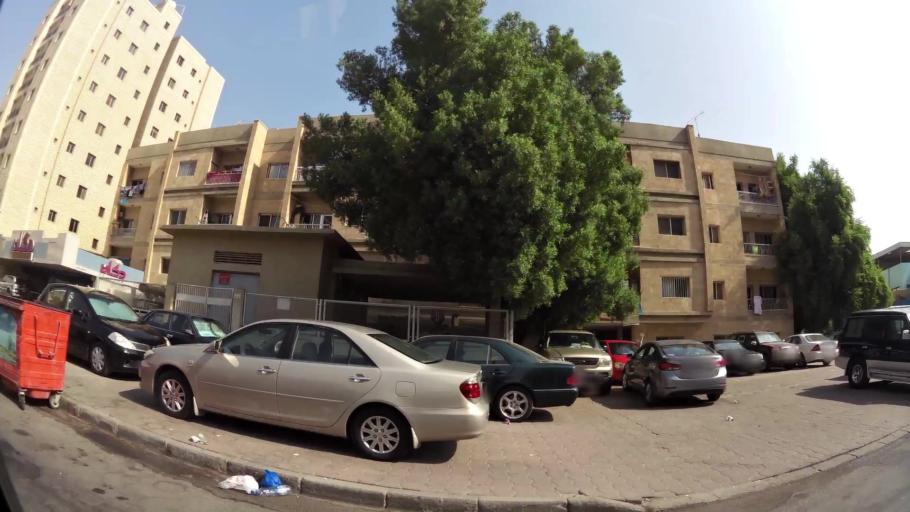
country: KW
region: Muhafazat Hawalli
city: Hawalli
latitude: 29.3346
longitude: 48.0326
